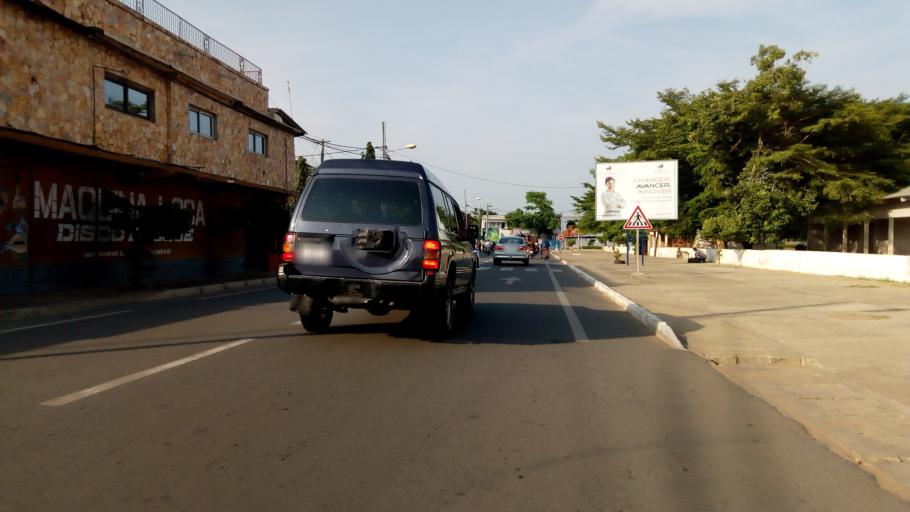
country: TG
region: Maritime
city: Lome
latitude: 6.1319
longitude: 1.2157
